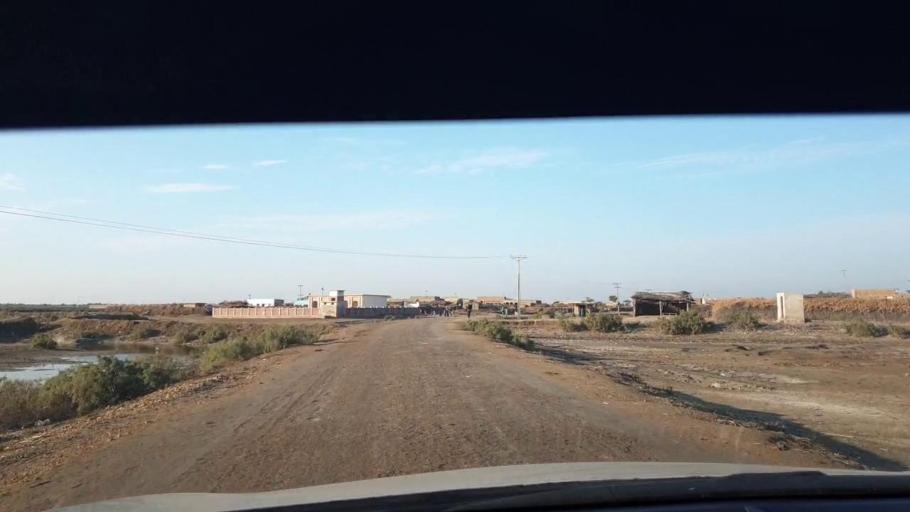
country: PK
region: Sindh
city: Berani
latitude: 25.8084
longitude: 68.9022
